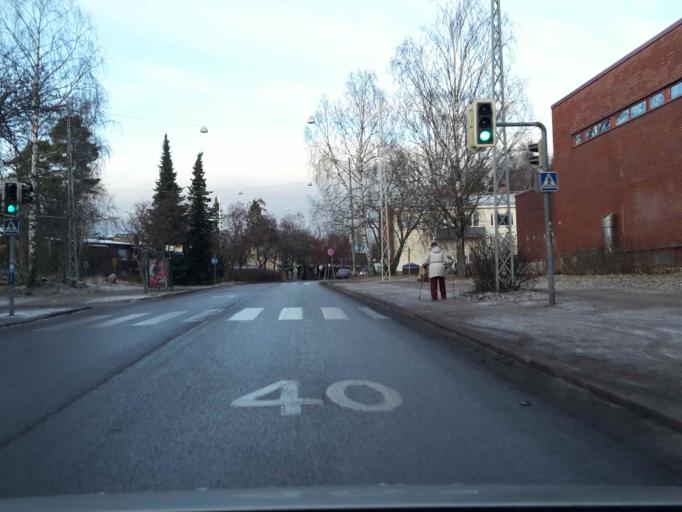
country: FI
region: Uusimaa
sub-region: Helsinki
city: Teekkarikylae
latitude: 60.1569
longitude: 24.8624
